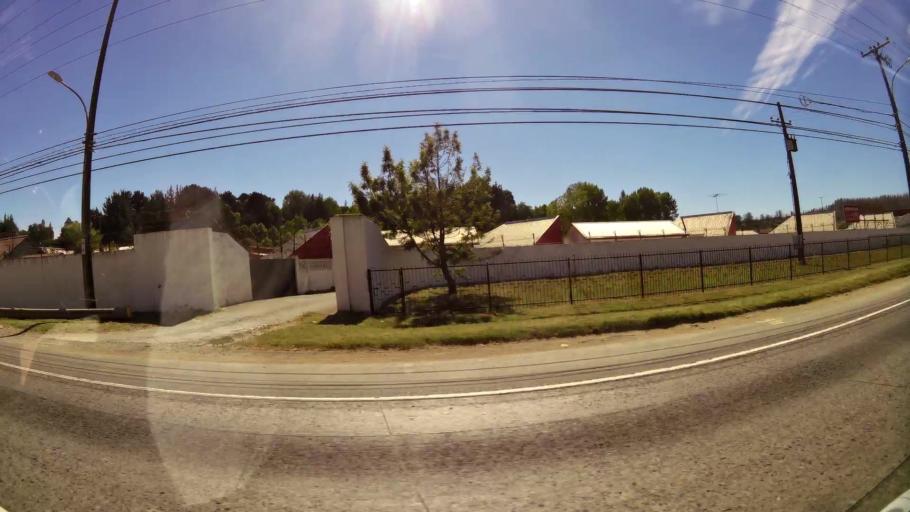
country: CL
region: Biobio
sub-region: Provincia de Concepcion
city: Penco
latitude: -36.7726
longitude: -73.0152
